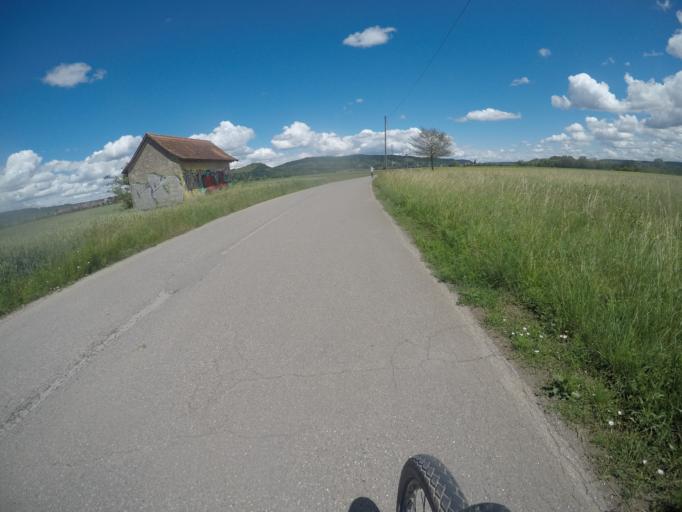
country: DE
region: Baden-Wuerttemberg
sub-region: Tuebingen Region
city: Rottenburg
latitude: 48.4858
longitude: 8.9690
